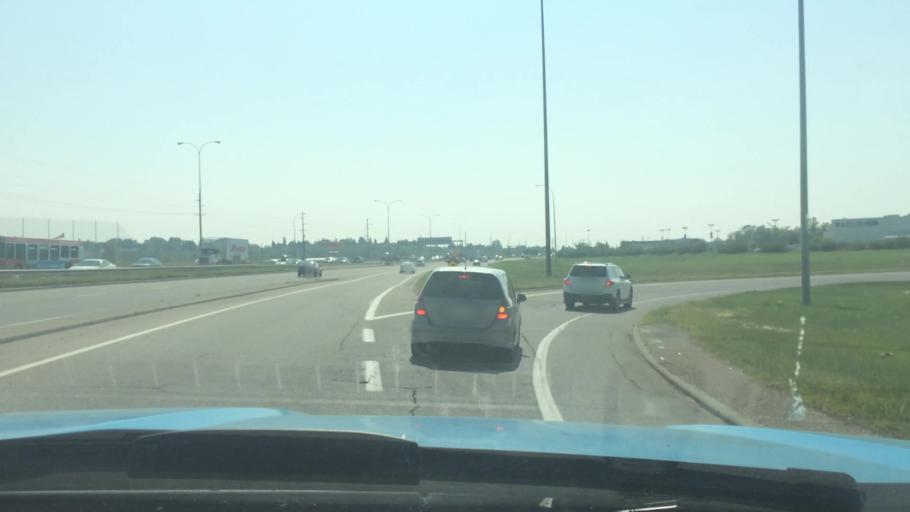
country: CA
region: Alberta
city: Calgary
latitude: 50.9925
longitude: -114.0336
